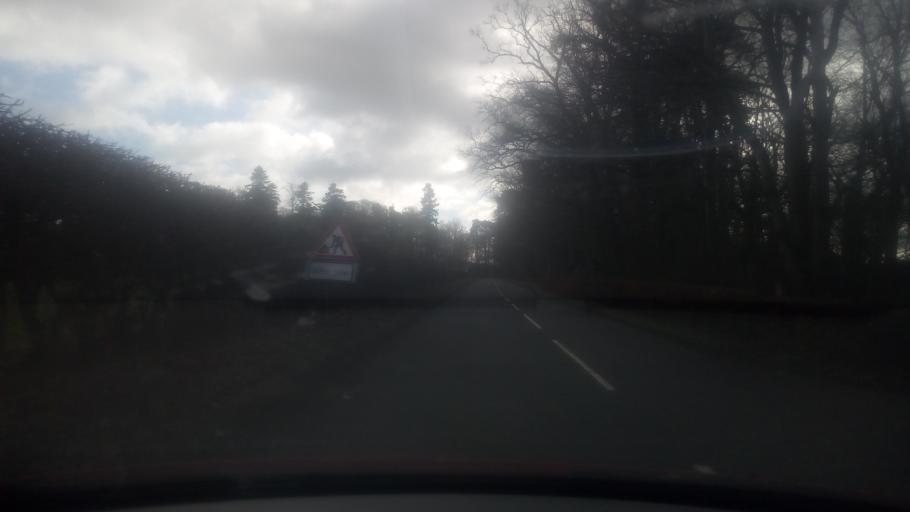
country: GB
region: Scotland
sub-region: The Scottish Borders
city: Saint Boswells
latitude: 55.5642
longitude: -2.6257
